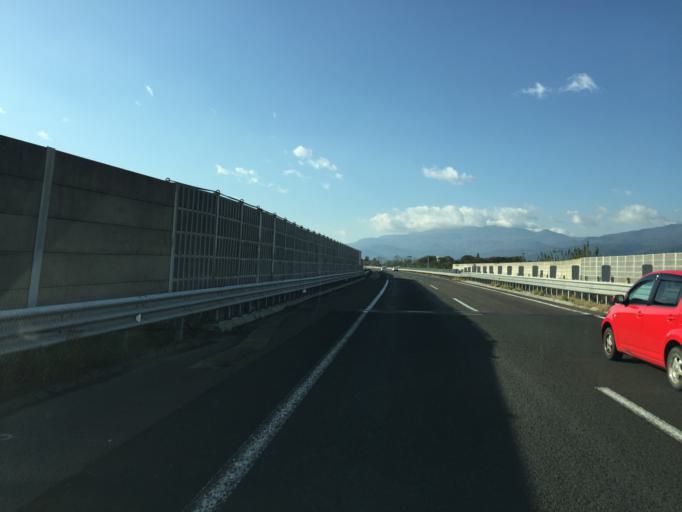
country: JP
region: Fukushima
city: Fukushima-shi
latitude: 37.7871
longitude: 140.4163
